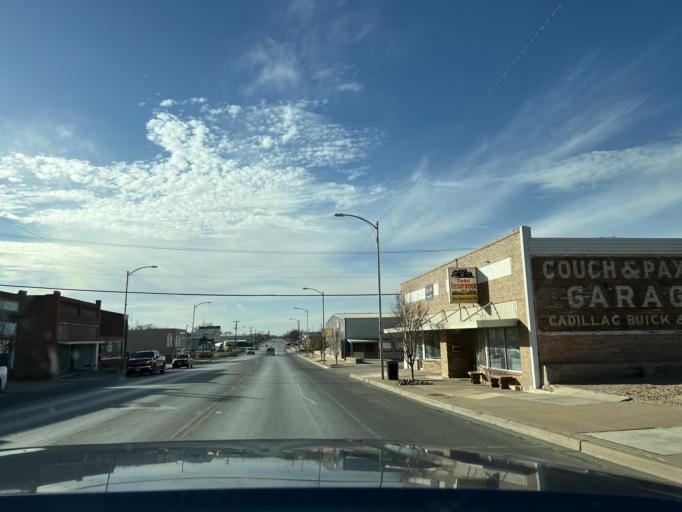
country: US
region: Texas
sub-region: Scurry County
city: Snyder
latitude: 32.7172
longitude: -100.9186
